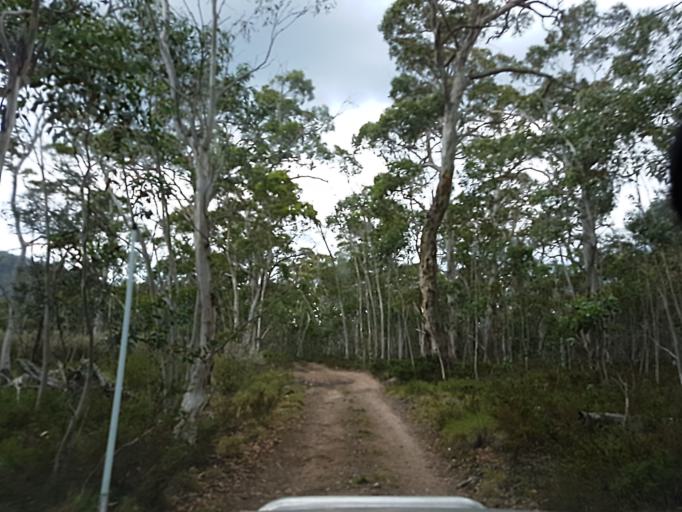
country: AU
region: New South Wales
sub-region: Snowy River
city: Jindabyne
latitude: -36.8780
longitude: 148.1603
